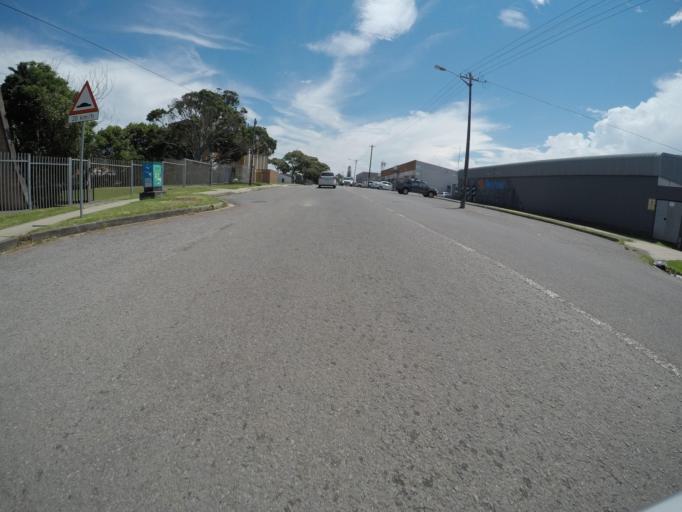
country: ZA
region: Eastern Cape
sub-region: Buffalo City Metropolitan Municipality
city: East London
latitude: -33.0353
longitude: 27.8611
